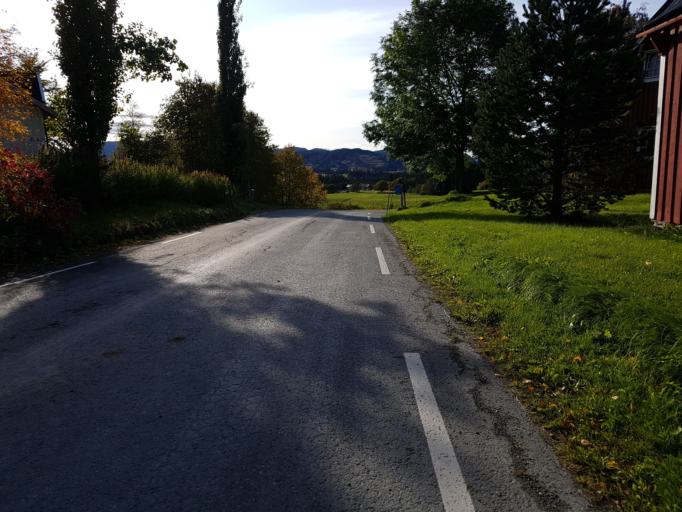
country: NO
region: Sor-Trondelag
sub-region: Klaebu
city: Klaebu
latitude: 63.3439
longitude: 10.5192
